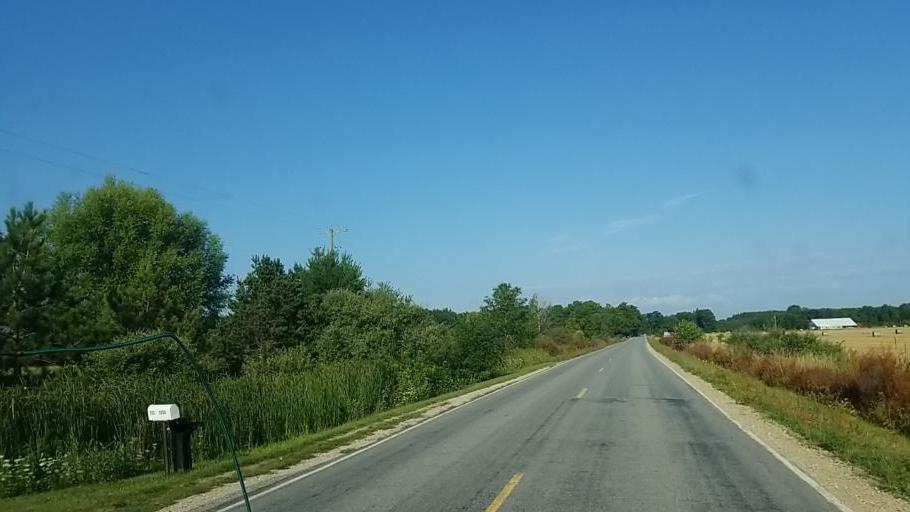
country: US
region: Michigan
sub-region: Newaygo County
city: Newaygo
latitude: 43.3508
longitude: -85.8996
